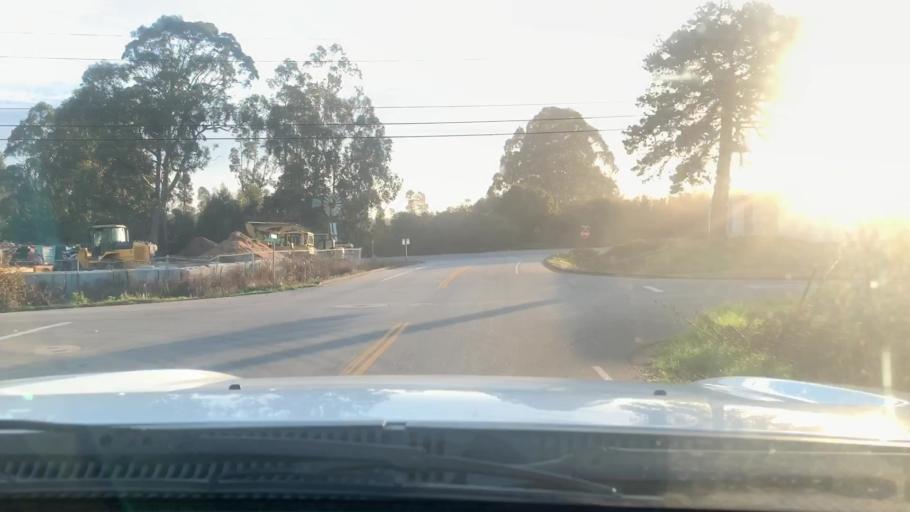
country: US
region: California
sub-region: San Luis Obispo County
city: Los Osos
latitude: 35.3127
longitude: -120.8246
